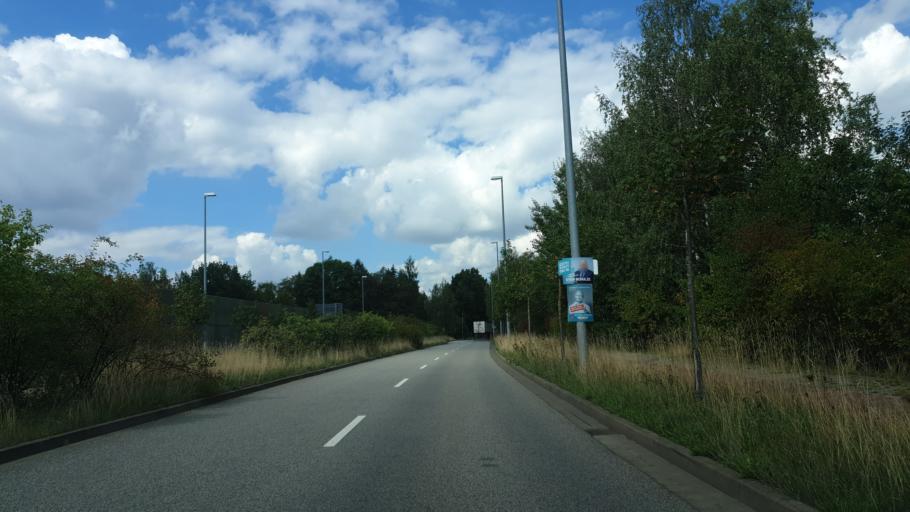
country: DE
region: Saxony
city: Neukirchen
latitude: 50.8129
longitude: 12.8747
